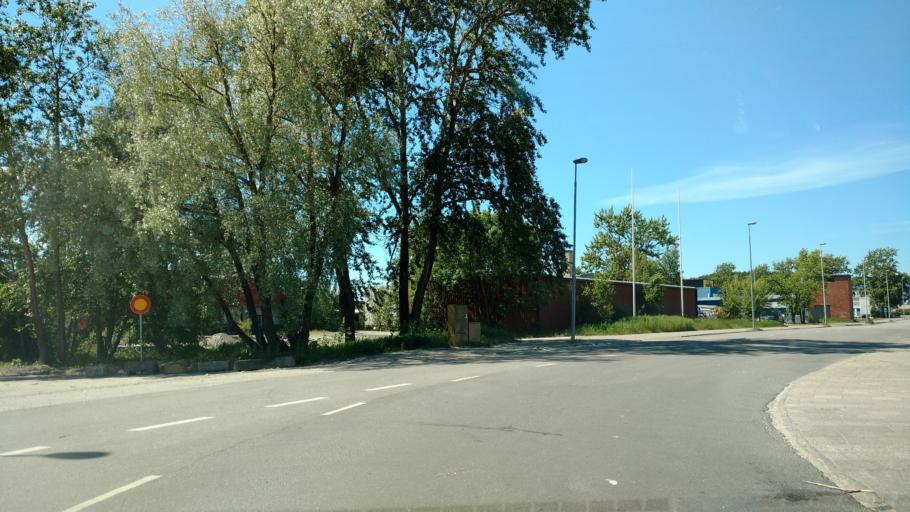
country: FI
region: Varsinais-Suomi
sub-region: Salo
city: Salo
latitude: 60.3899
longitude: 23.1165
